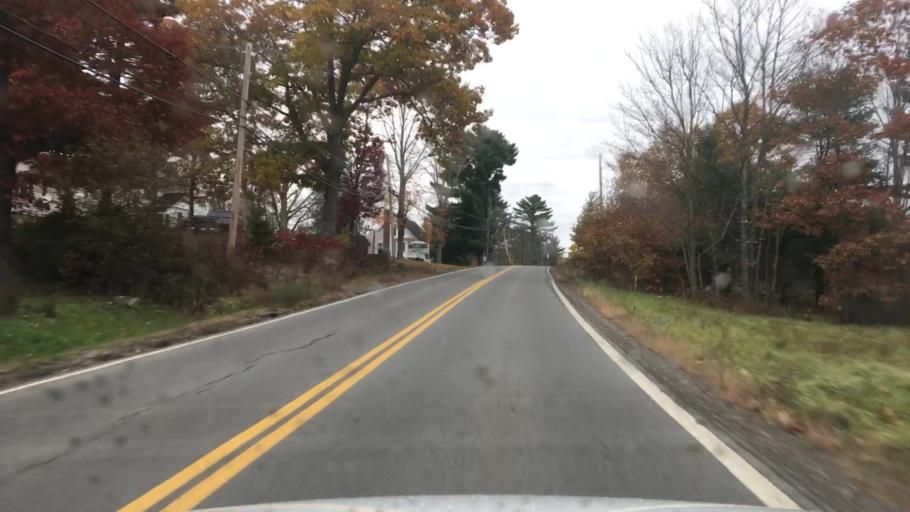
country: US
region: Maine
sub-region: Lincoln County
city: Jefferson
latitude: 44.2044
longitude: -69.4756
